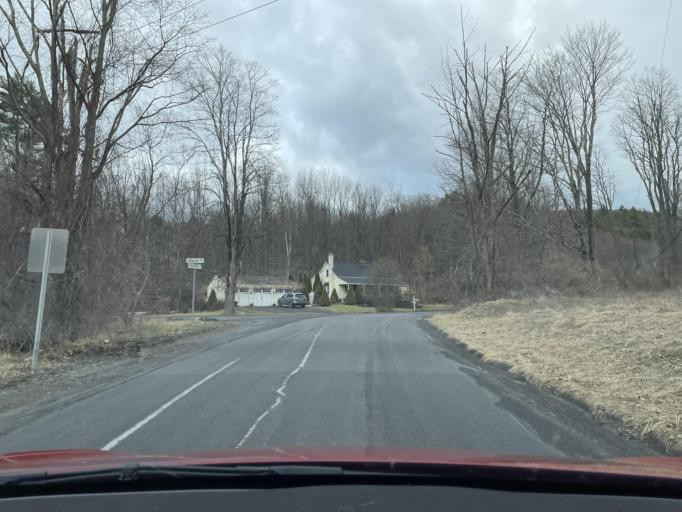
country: US
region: New York
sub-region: Ulster County
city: Woodstock
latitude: 42.0665
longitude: -74.1612
